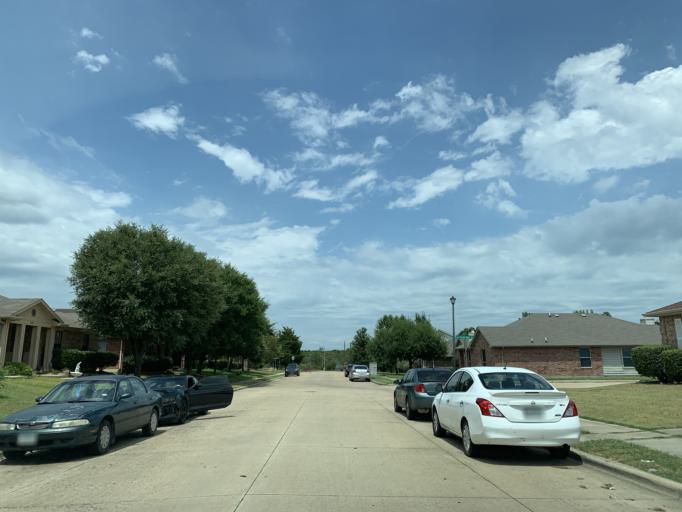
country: US
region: Texas
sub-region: Dallas County
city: DeSoto
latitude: 32.6606
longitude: -96.8114
